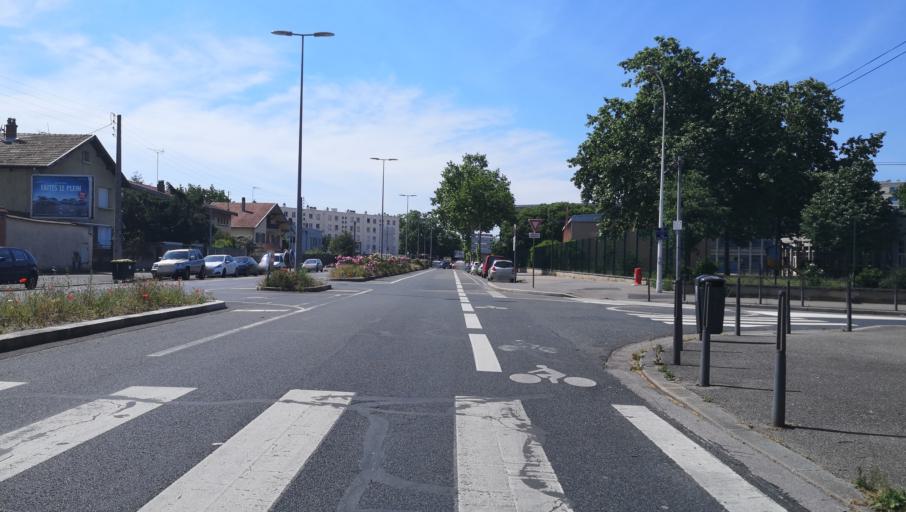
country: FR
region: Rhone-Alpes
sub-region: Departement du Rhone
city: Saint-Fons
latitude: 45.7264
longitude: 4.8647
